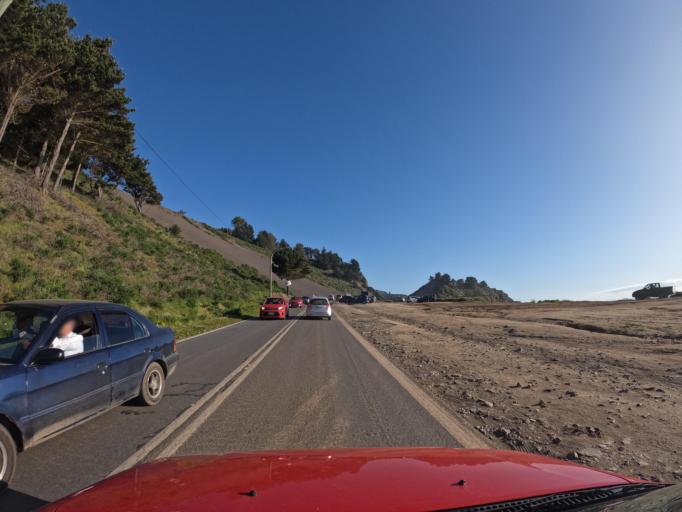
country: CL
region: Maule
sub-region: Provincia de Talca
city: Constitucion
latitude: -35.3370
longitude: -72.4339
